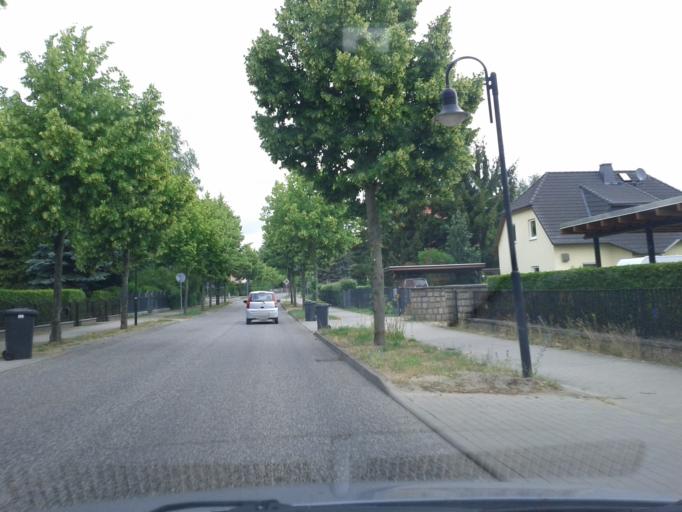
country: DE
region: Brandenburg
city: Woltersdorf
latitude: 52.4545
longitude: 13.7488
